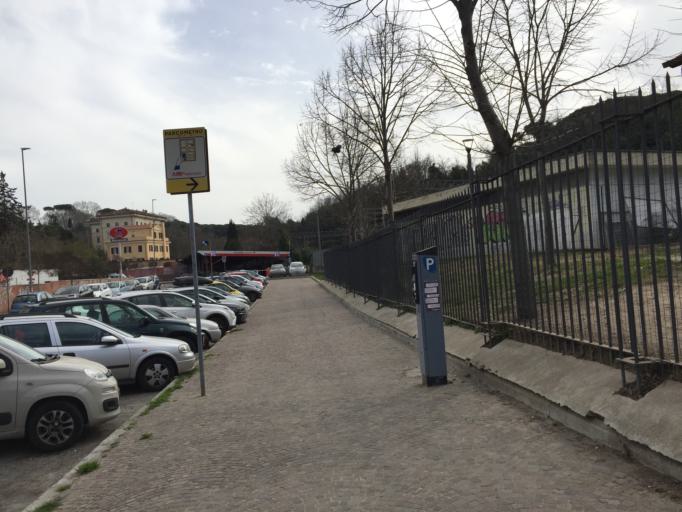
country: VA
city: Vatican City
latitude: 41.8953
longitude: 12.4561
